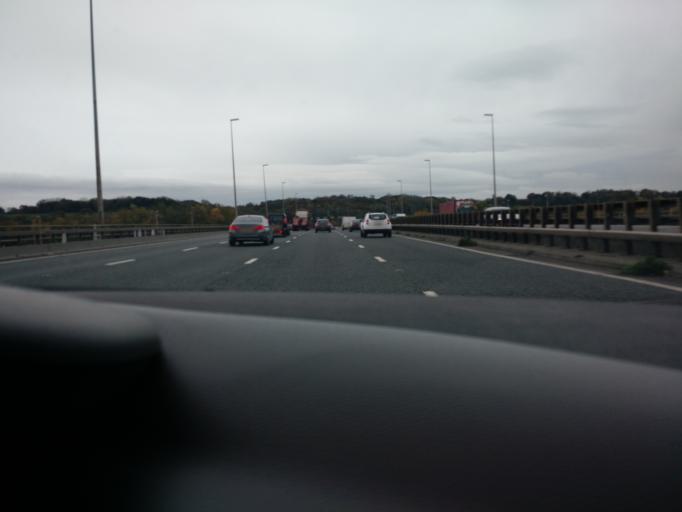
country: GB
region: England
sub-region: Lancashire
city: Goosnargh
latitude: 53.7664
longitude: -2.6362
